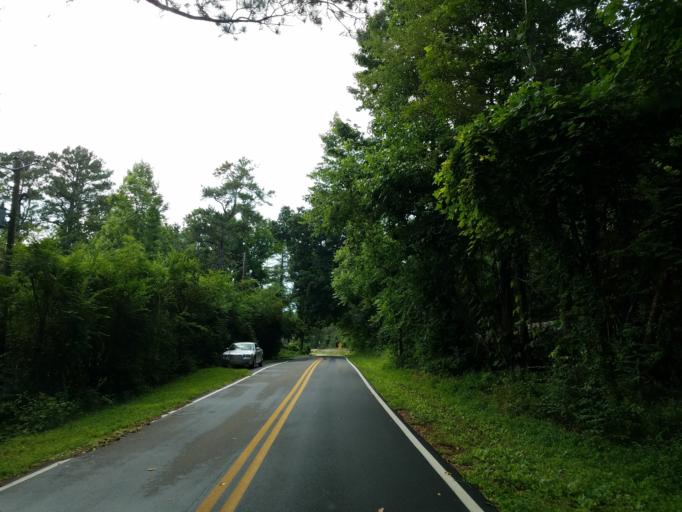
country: US
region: Georgia
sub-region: Pickens County
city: Jasper
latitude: 34.4619
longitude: -84.4141
